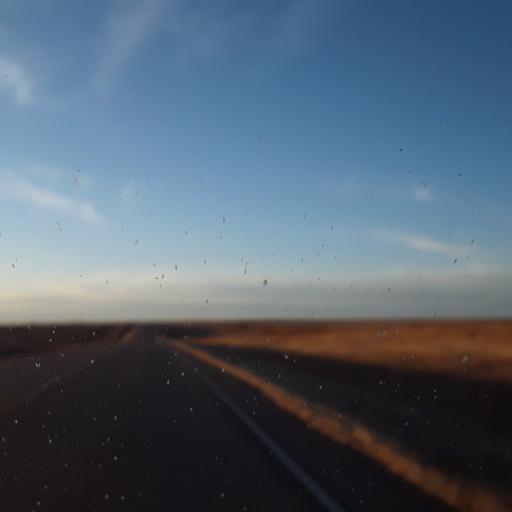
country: US
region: Colorado
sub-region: Cheyenne County
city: Cheyenne Wells
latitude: 38.8145
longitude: -102.4782
